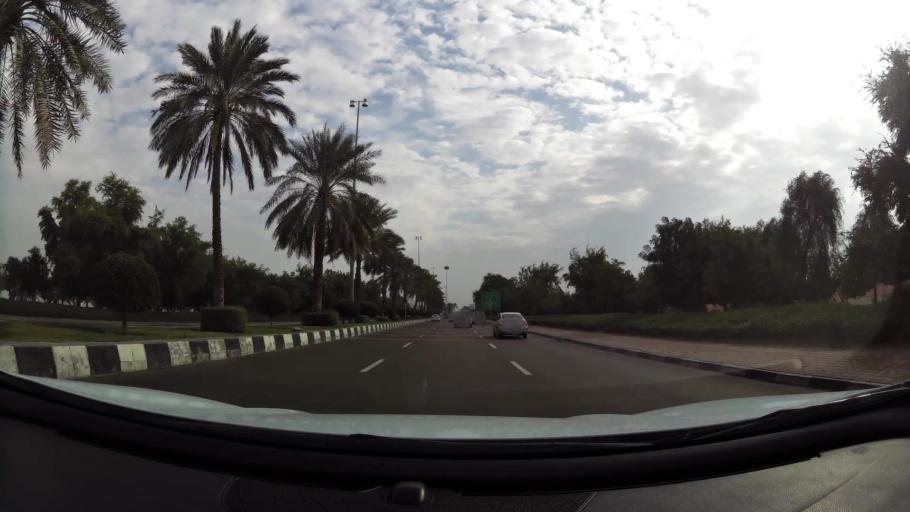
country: AE
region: Abu Dhabi
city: Al Ain
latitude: 24.1930
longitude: 55.6516
